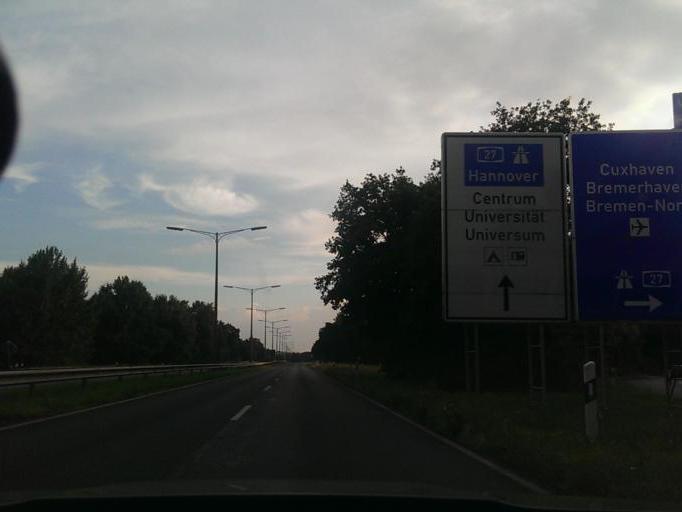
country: DE
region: Lower Saxony
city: Lilienthal
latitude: 53.1130
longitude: 8.8697
